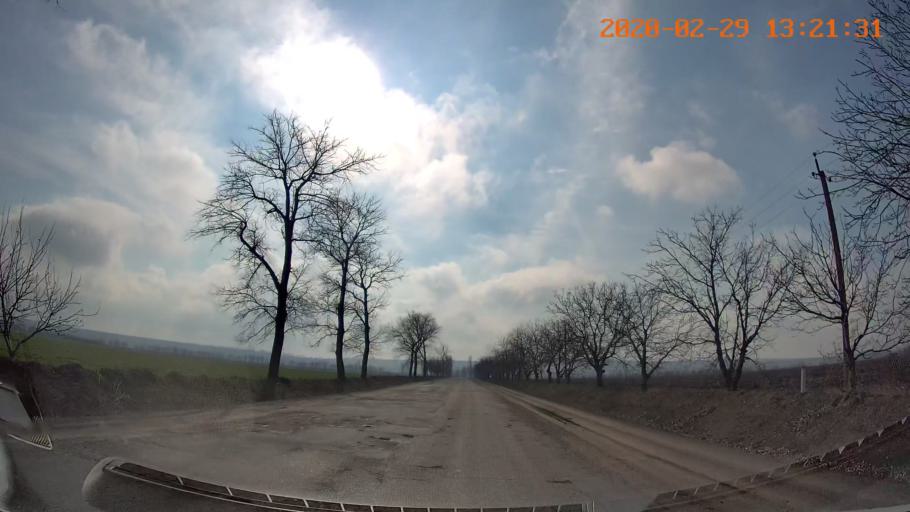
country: MD
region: Telenesti
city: Camenca
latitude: 47.9695
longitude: 28.6323
